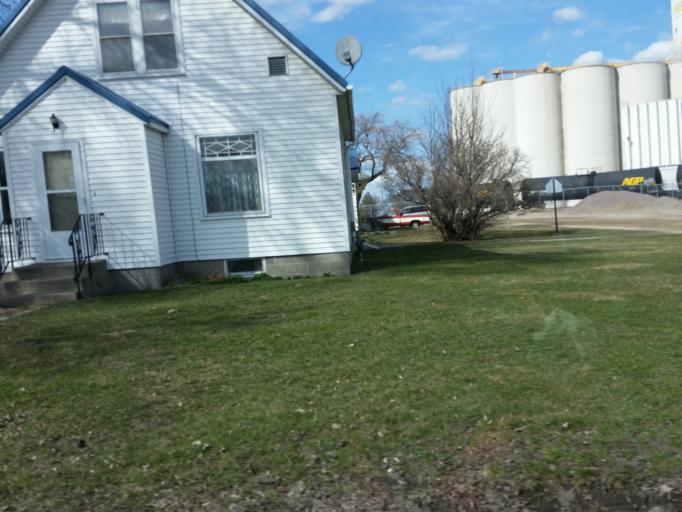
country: US
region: Minnesota
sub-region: Lac qui Parle County
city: Dawson
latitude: 44.9319
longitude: -96.0589
